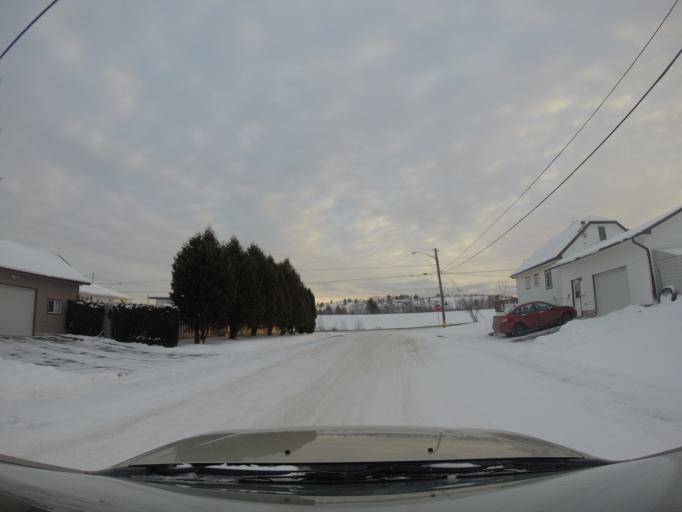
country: CA
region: Ontario
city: Greater Sudbury
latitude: 46.4865
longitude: -80.8586
